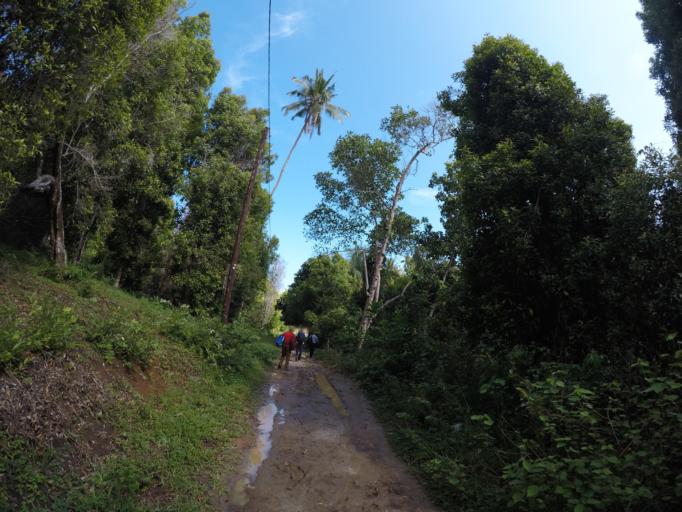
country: TZ
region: Pemba South
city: Mtambile
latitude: -5.3834
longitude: 39.7202
